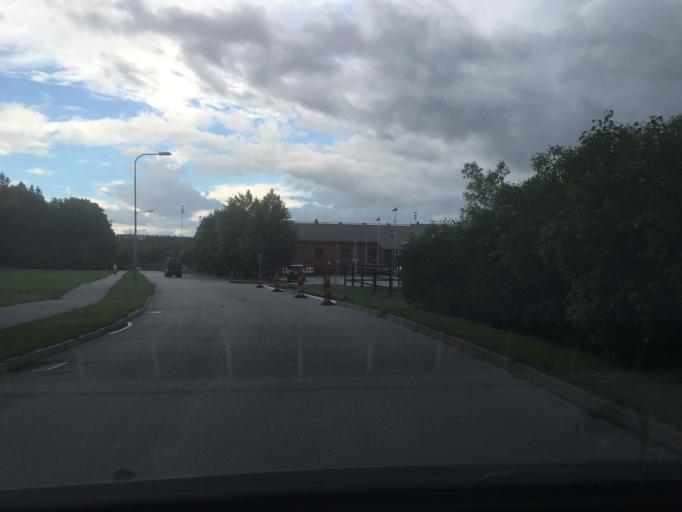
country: SE
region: Stockholm
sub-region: Stockholms Kommun
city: Bromma
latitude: 59.3396
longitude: 17.9261
